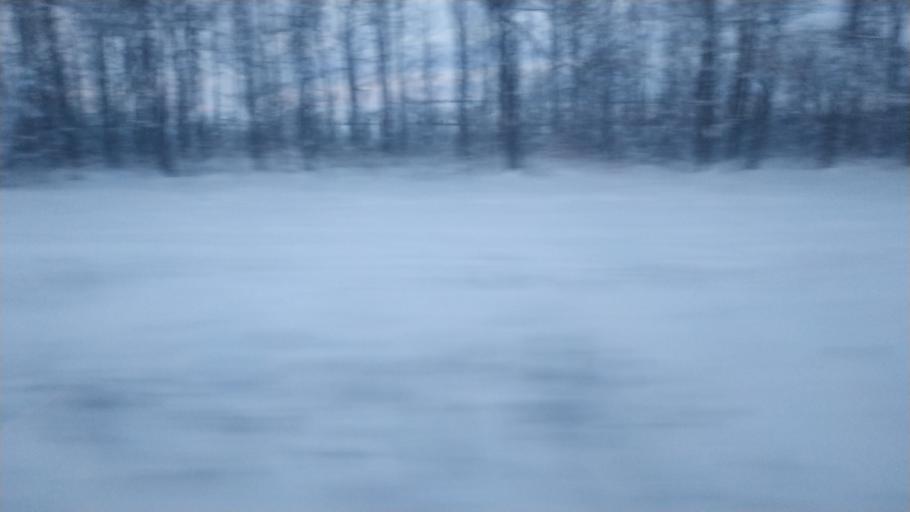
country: RU
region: Tatarstan
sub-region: Arskiy Rayon
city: Arsk
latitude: 56.0187
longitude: 49.6307
